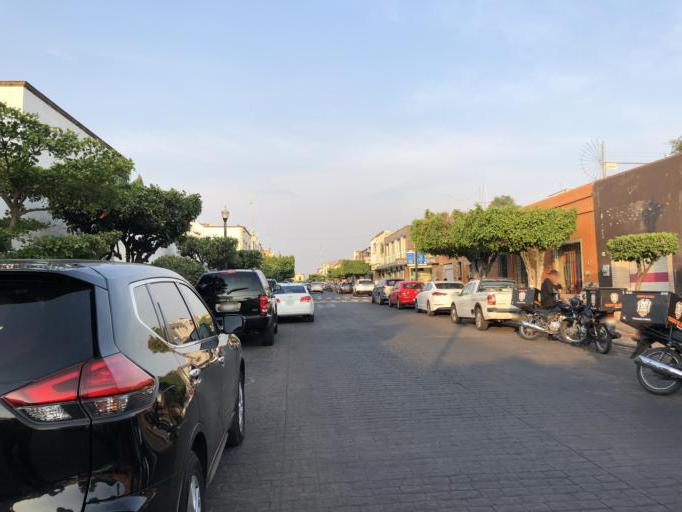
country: MX
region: Jalisco
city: Tlaquepaque
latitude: 20.6385
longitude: -103.3141
